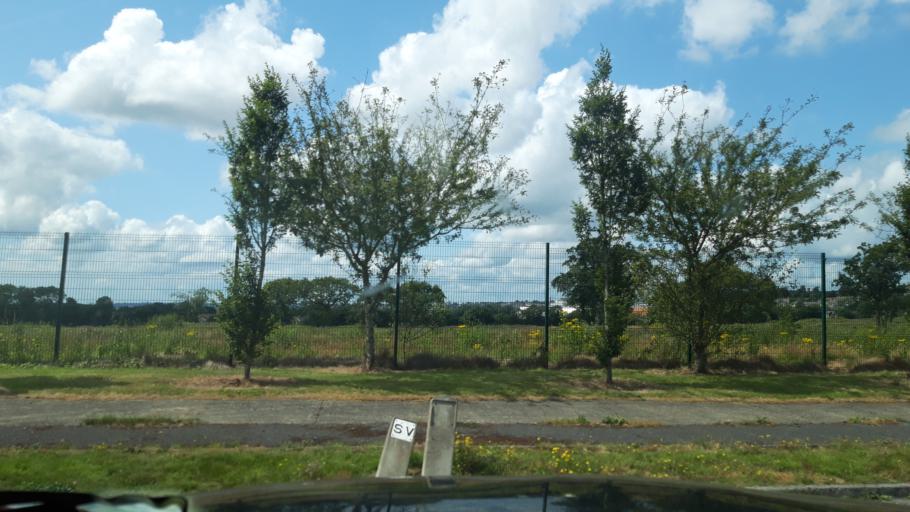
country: IE
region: Munster
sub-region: Waterford
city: Waterford
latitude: 52.2692
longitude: -7.0863
